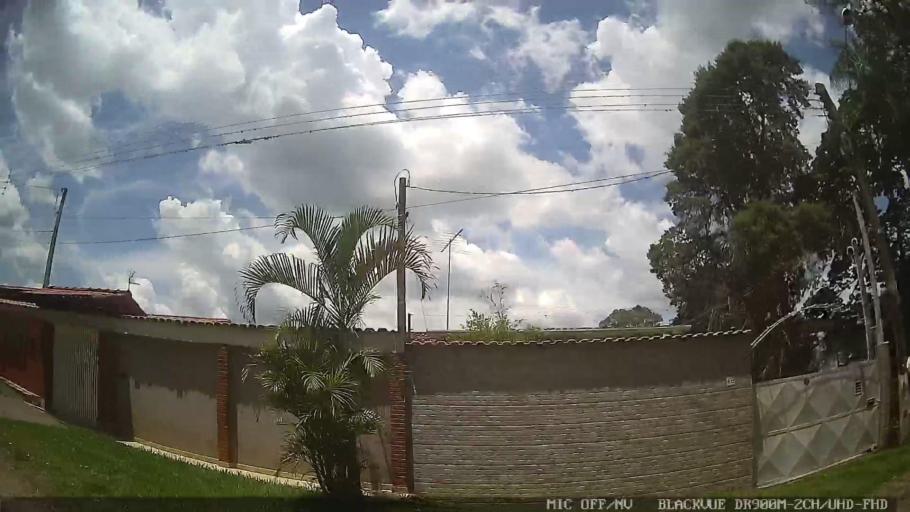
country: BR
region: Sao Paulo
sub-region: Atibaia
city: Atibaia
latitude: -23.0985
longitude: -46.6349
